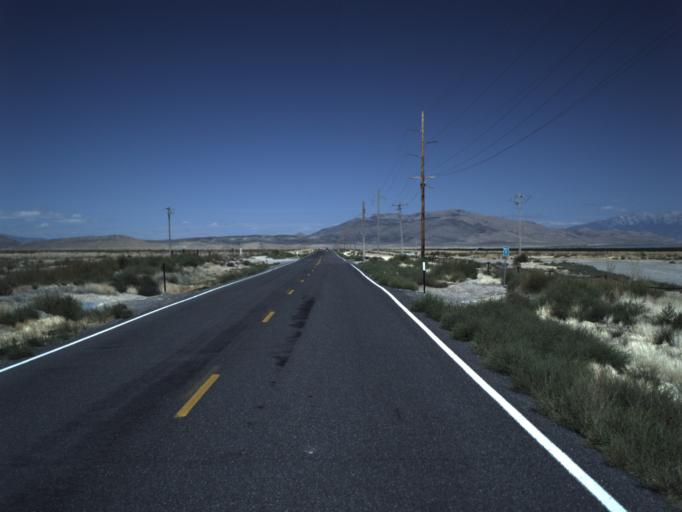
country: US
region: Utah
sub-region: Utah County
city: Genola
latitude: 40.0532
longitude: -111.9583
